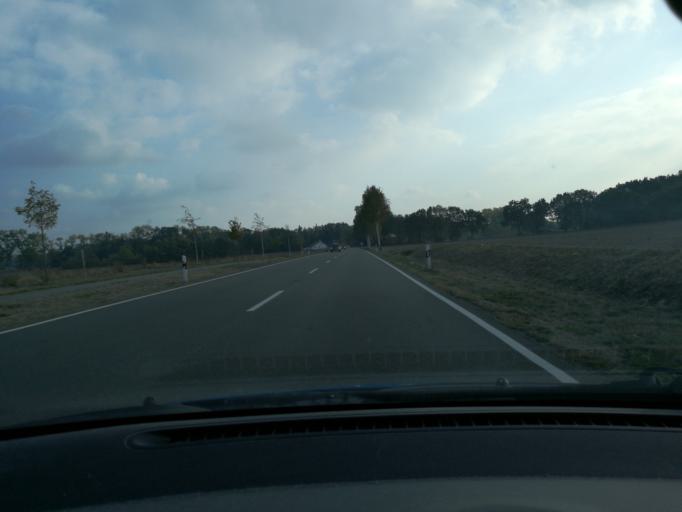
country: DE
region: Lower Saxony
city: Dannenberg
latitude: 53.0929
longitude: 11.0649
